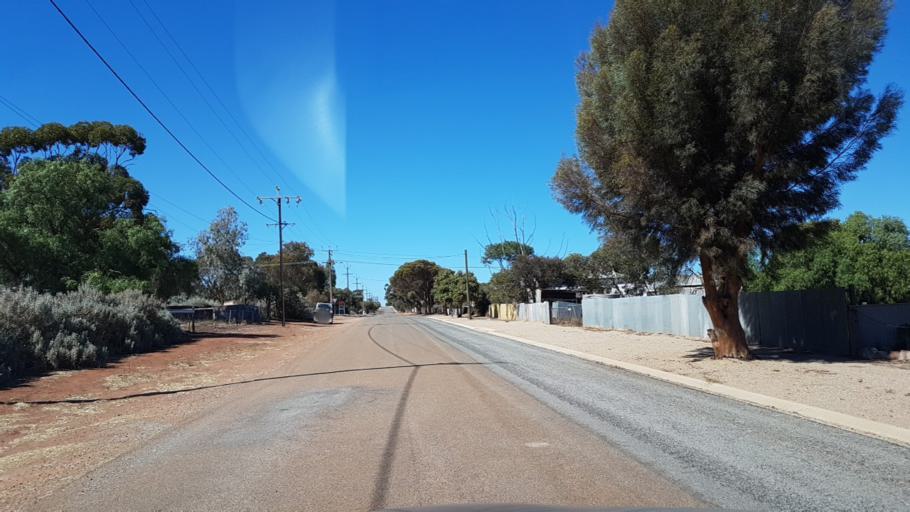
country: AU
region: South Australia
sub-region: Peterborough
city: Peterborough
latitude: -32.9710
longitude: 138.8273
